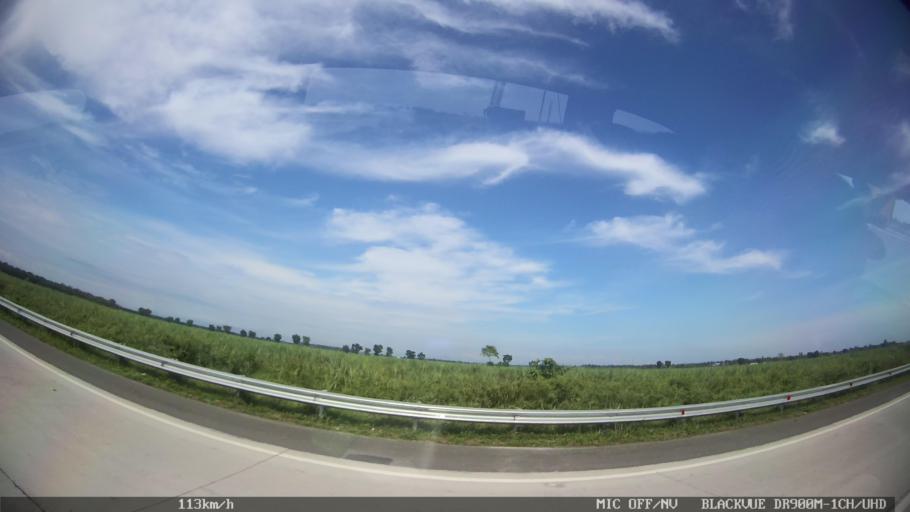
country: ID
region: North Sumatra
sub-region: Kabupaten Langkat
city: Stabat
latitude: 3.6930
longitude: 98.5407
